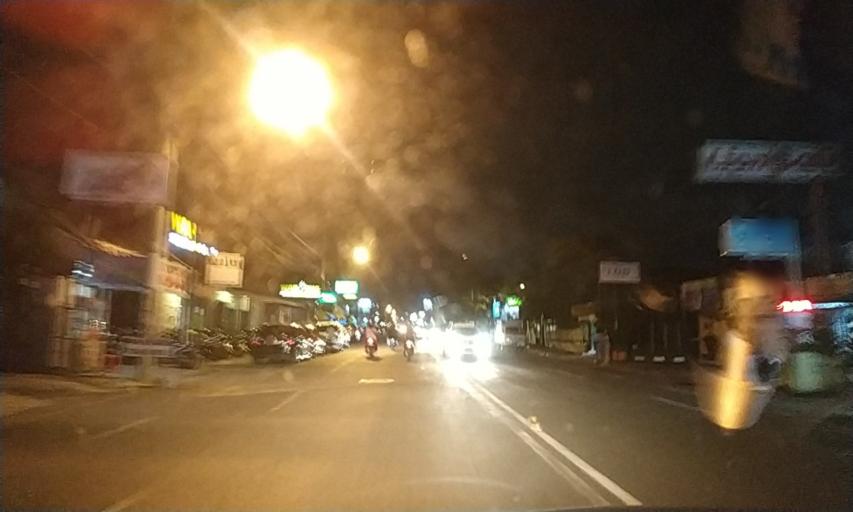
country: ID
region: Daerah Istimewa Yogyakarta
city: Yogyakarta
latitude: -7.7982
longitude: 110.3524
